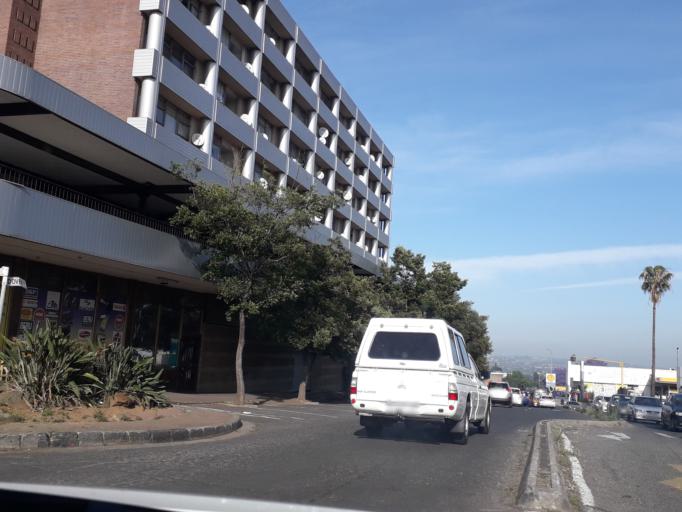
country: ZA
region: Gauteng
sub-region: City of Johannesburg Metropolitan Municipality
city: Johannesburg
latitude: -26.0903
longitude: 28.0079
